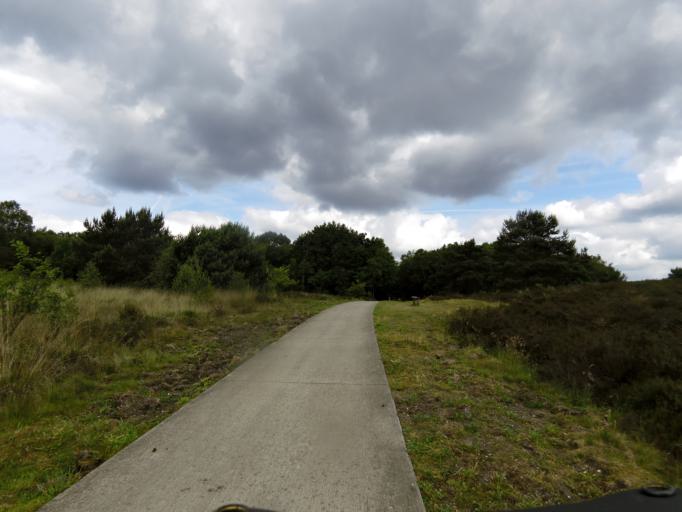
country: NL
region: Gelderland
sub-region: Gemeente Apeldoorn
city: Uddel
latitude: 52.3150
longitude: 5.7619
